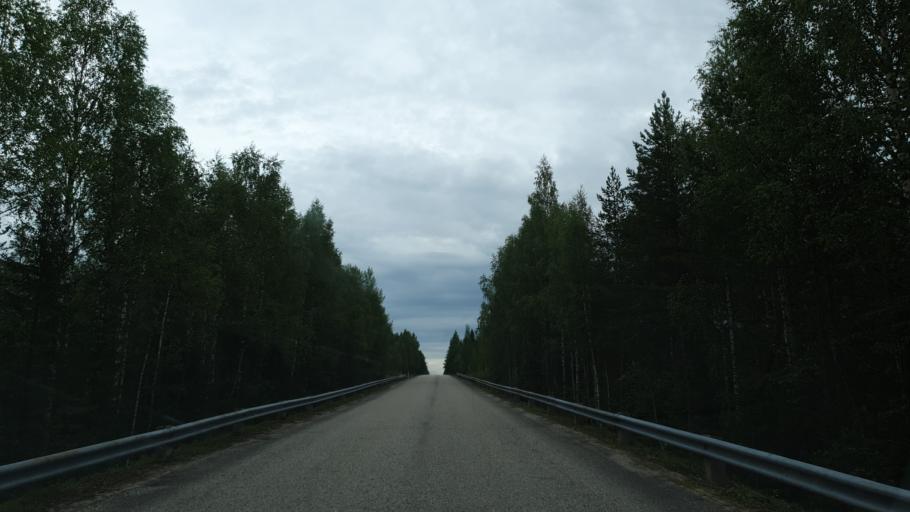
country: FI
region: Kainuu
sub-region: Kehys-Kainuu
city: Kuhmo
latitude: 64.3517
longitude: 29.1113
